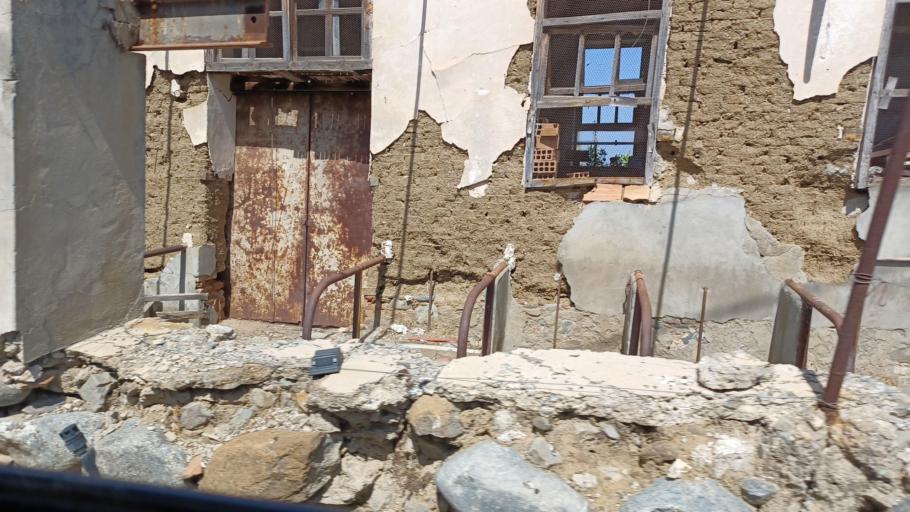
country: CY
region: Lefkosia
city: Lefka
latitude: 35.0615
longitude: 32.8871
